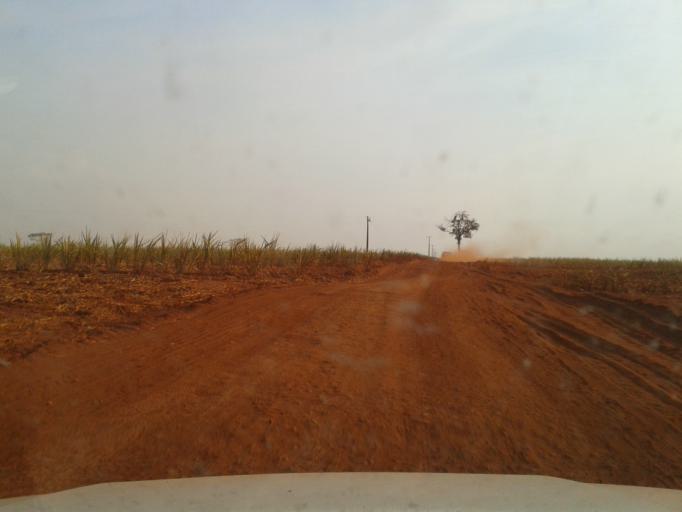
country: BR
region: Minas Gerais
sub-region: Capinopolis
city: Capinopolis
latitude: -18.7315
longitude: -49.6864
